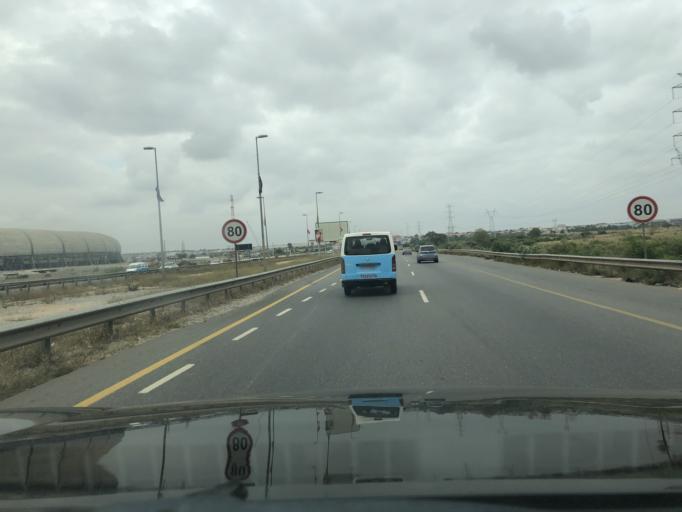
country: AO
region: Luanda
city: Luanda
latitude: -8.9725
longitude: 13.2791
